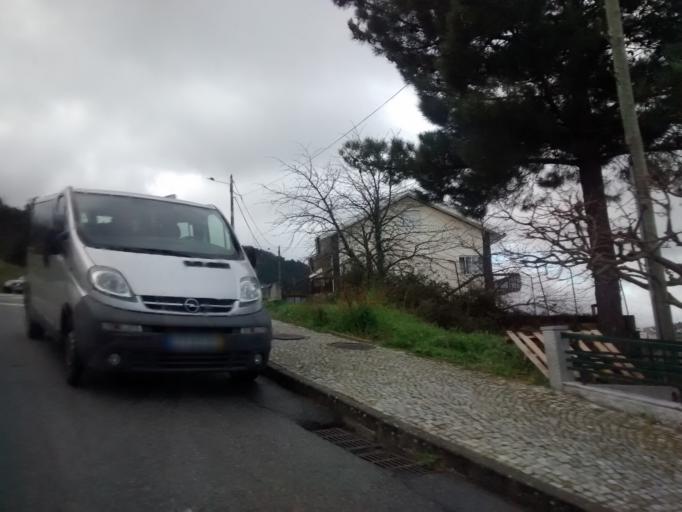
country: PT
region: Guarda
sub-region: Seia
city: Seia
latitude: 40.4133
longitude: -7.7039
